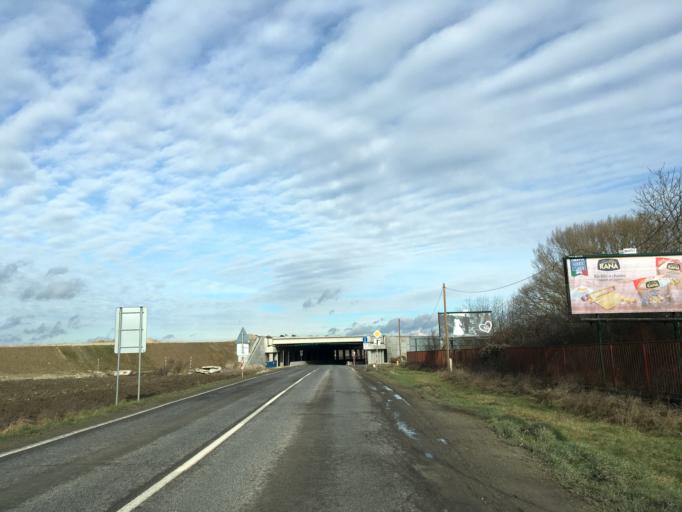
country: AT
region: Burgenland
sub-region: Politischer Bezirk Neusiedl am See
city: Kittsee
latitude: 48.0730
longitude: 17.1192
